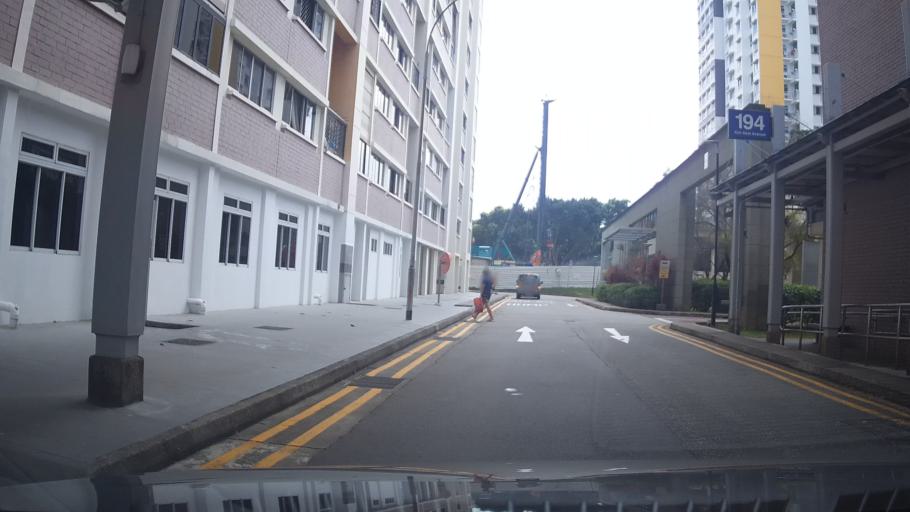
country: SG
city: Singapore
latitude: 1.3315
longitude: 103.8580
